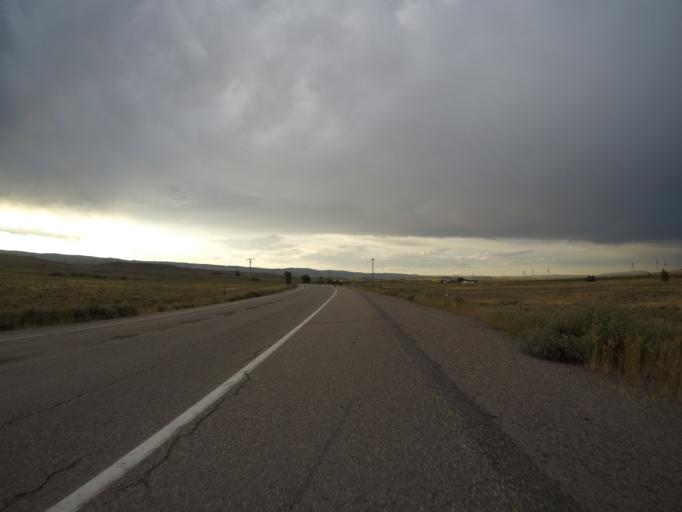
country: US
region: Idaho
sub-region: Bear Lake County
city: Montpelier
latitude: 42.0703
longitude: -110.9438
